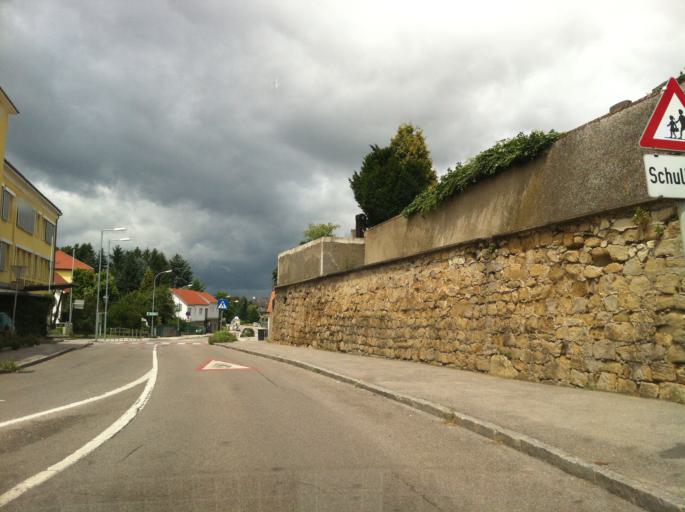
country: AT
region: Lower Austria
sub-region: Politischer Bezirk Tulln
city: Sieghartskirchen
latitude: 48.2554
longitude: 16.0111
